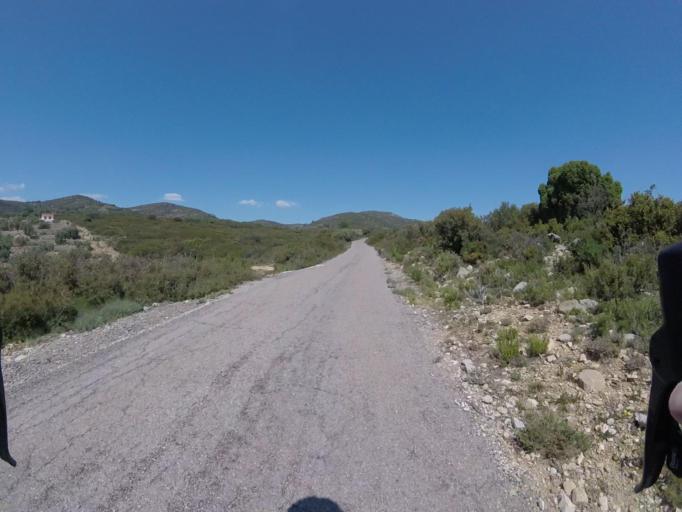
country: ES
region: Valencia
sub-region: Provincia de Castello
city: Sierra-Engarceran
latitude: 40.2449
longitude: -0.0277
